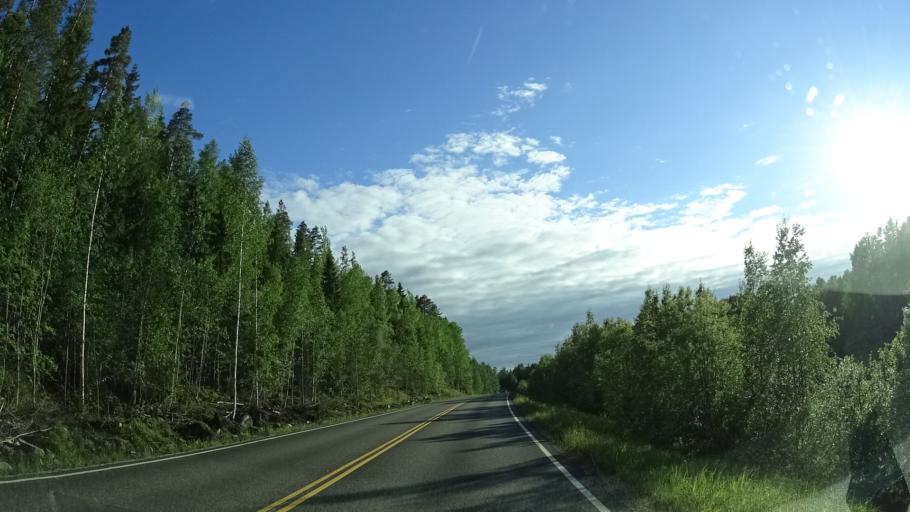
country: FI
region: Paijanne Tavastia
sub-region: Lahti
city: Asikkala
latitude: 61.3393
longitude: 25.5904
